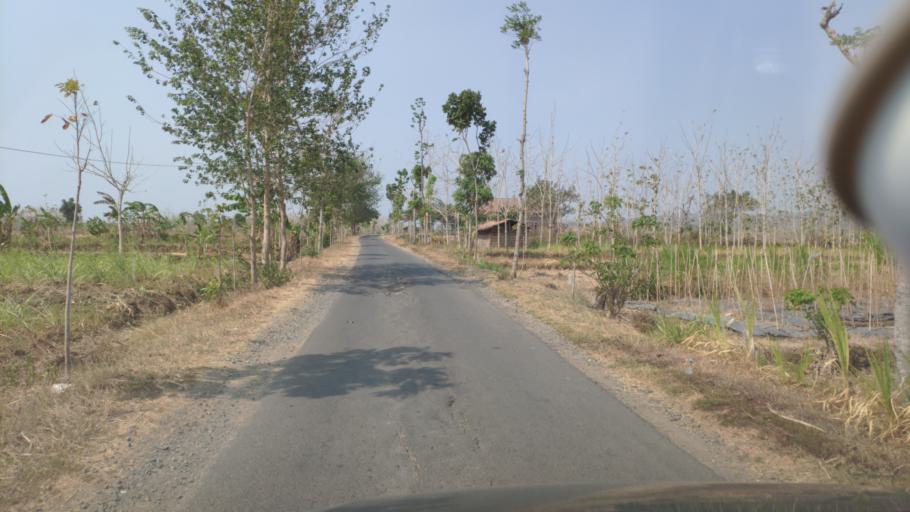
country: ID
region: Central Java
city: Karanggeneng
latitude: -6.9206
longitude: 111.4518
